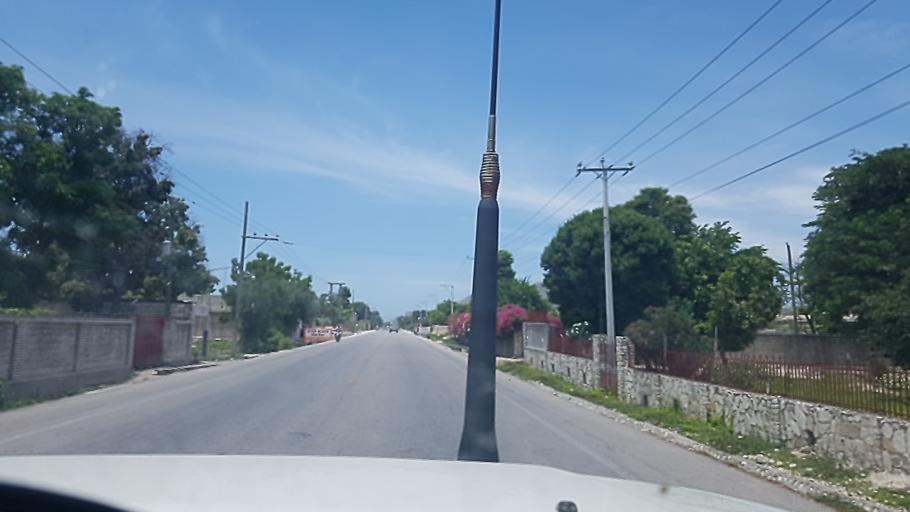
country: HT
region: Artibonite
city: Gonayiv
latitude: 19.4885
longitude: -72.6504
